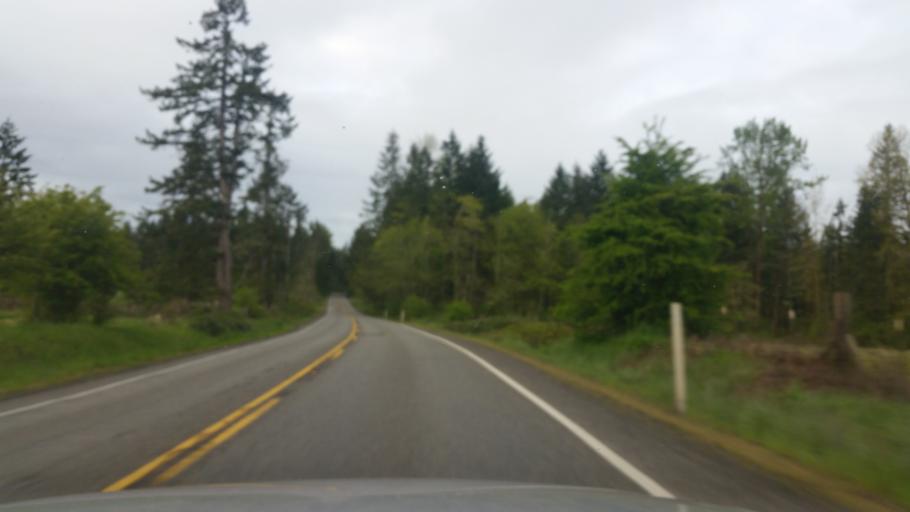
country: US
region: Washington
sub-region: Pierce County
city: Eatonville
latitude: 46.9198
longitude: -122.2889
